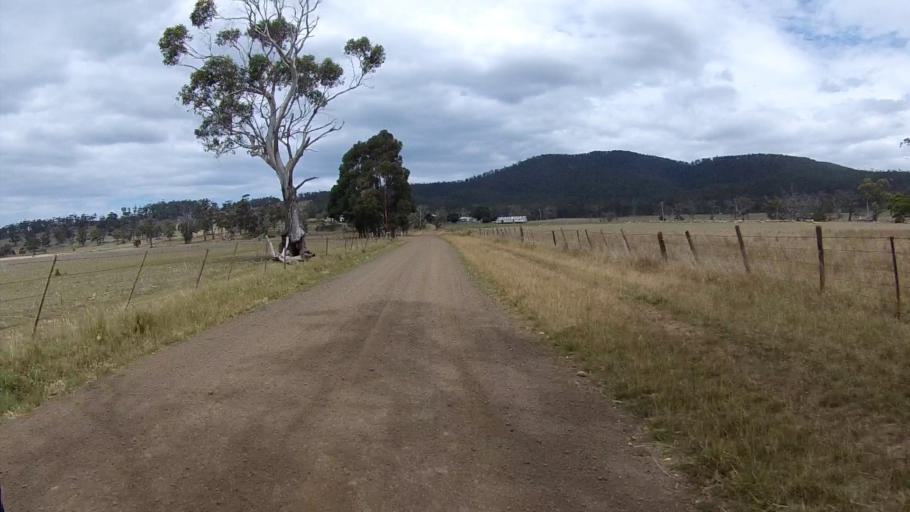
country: AU
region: Tasmania
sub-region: Sorell
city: Sorell
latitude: -42.6572
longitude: 147.9402
